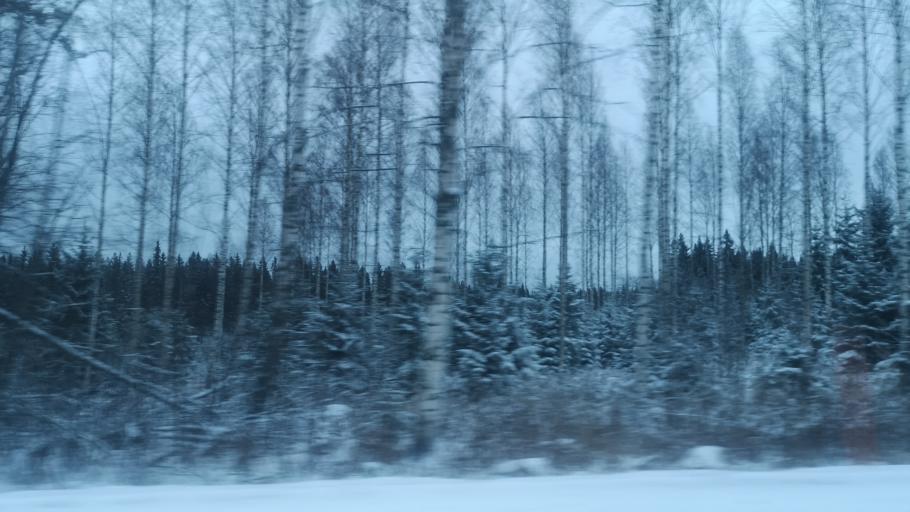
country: FI
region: Southern Savonia
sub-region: Savonlinna
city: Savonlinna
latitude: 62.0092
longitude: 28.7345
